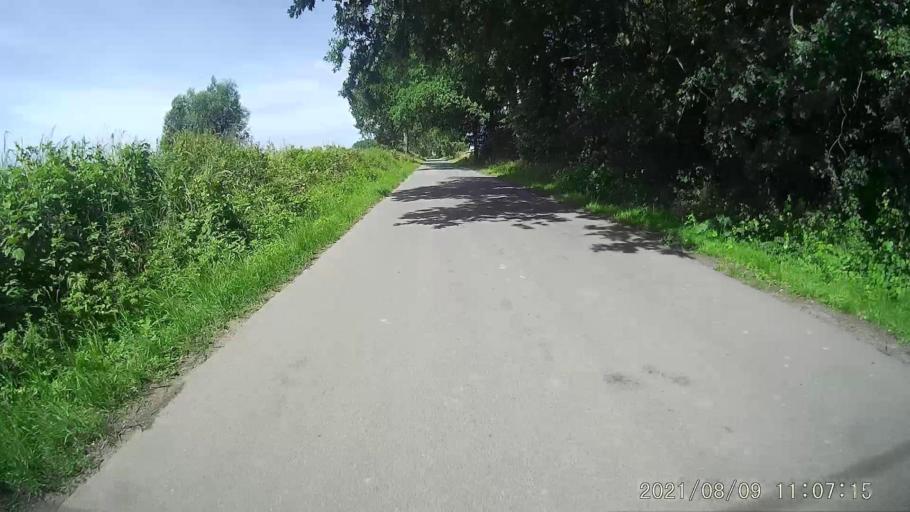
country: PL
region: Lower Silesian Voivodeship
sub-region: Powiat klodzki
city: Bozkow
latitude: 50.4563
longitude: 16.5965
